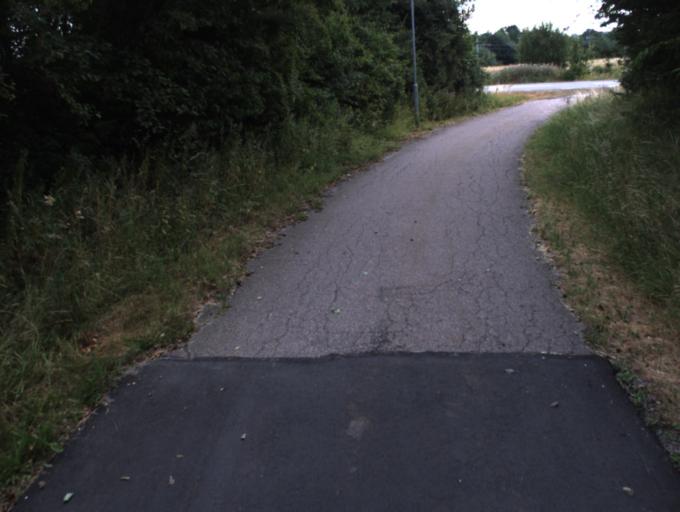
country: SE
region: Skane
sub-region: Helsingborg
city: Gantofta
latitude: 56.0201
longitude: 12.7620
